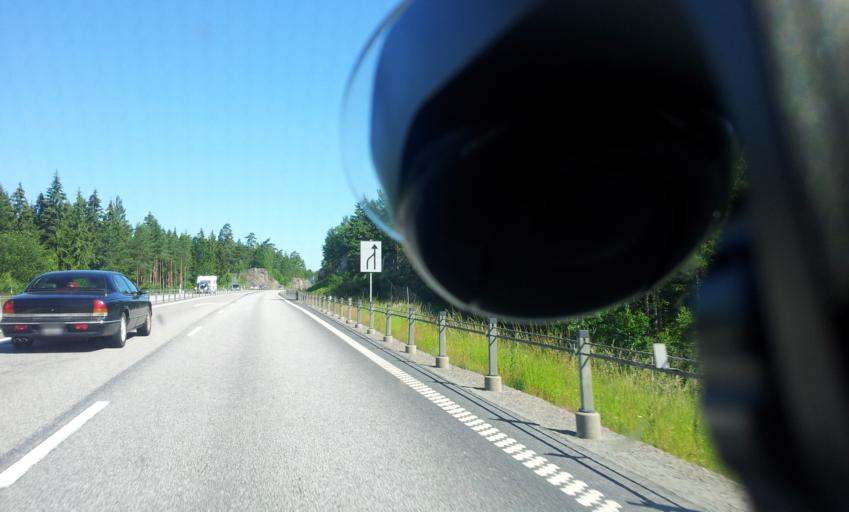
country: SE
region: OEstergoetland
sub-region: Valdemarsviks Kommun
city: Gusum
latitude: 58.3448
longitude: 16.4489
